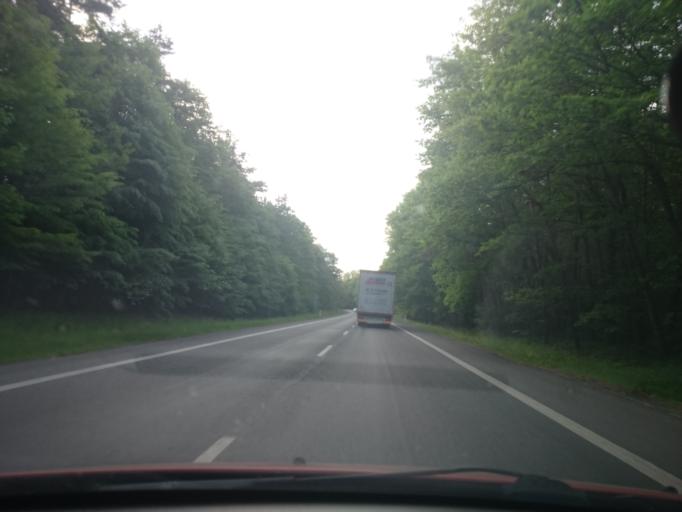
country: PL
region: Opole Voivodeship
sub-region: Powiat opolski
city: Tarnow Opolski
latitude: 50.6142
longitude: 18.0664
